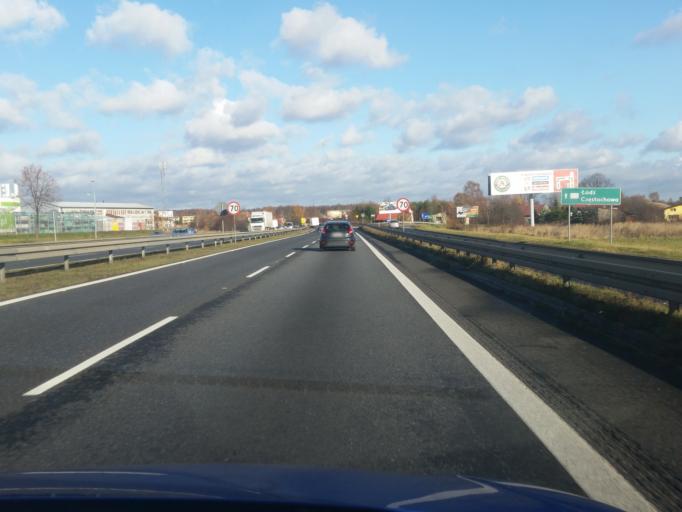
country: PL
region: Silesian Voivodeship
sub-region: Powiat czestochowski
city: Huta Stara B
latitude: 50.7313
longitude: 19.1618
